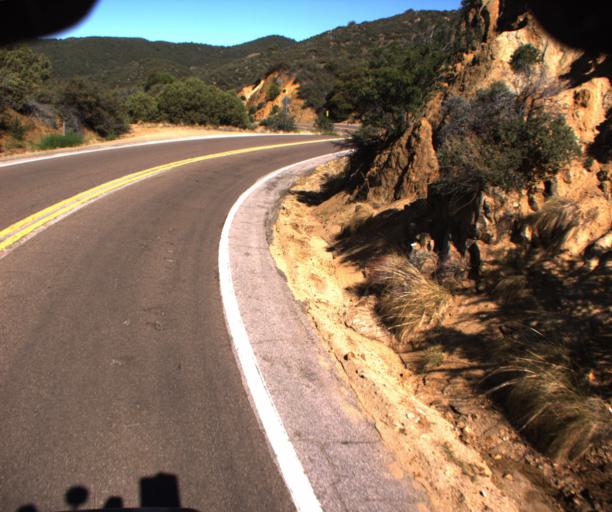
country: US
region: Arizona
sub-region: Yavapai County
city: Prescott
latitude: 34.4536
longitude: -112.5265
